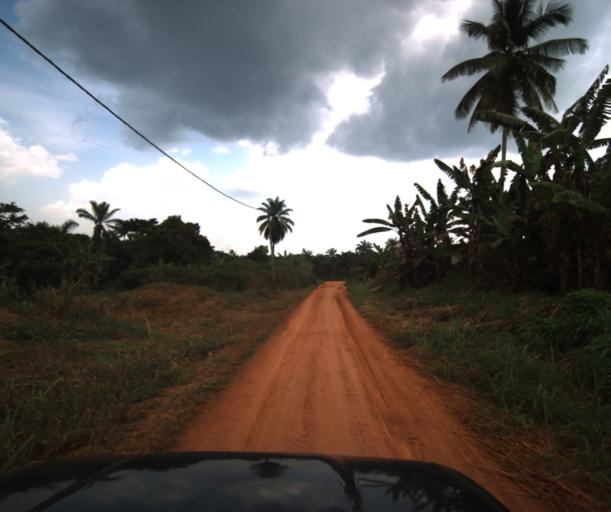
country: CM
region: Centre
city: Akono
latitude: 3.5976
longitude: 11.1765
